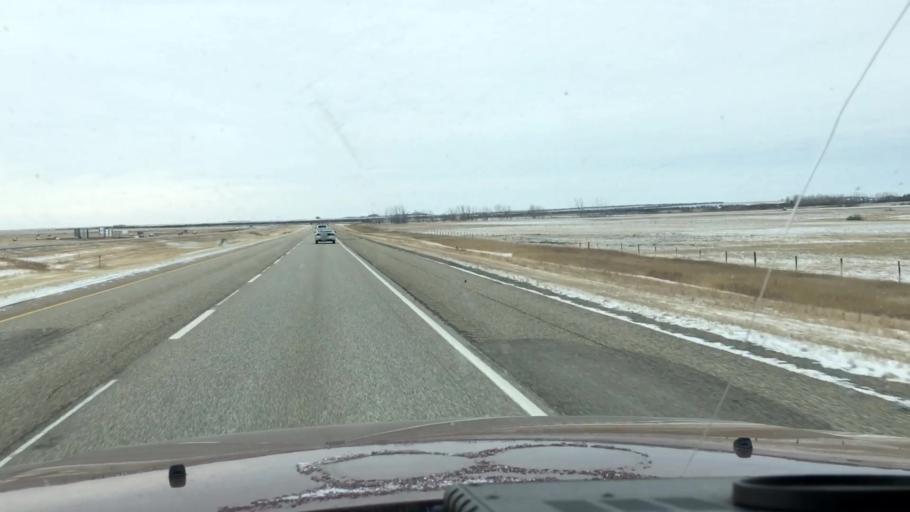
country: CA
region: Saskatchewan
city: Saskatoon
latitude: 51.4837
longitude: -106.2506
